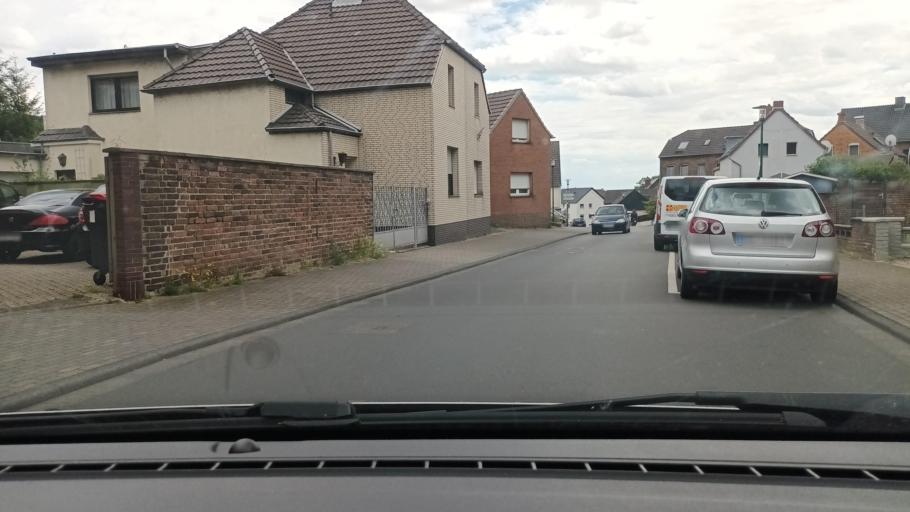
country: DE
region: North Rhine-Westphalia
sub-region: Regierungsbezirk Koln
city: Hurth
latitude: 50.8633
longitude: 6.8801
